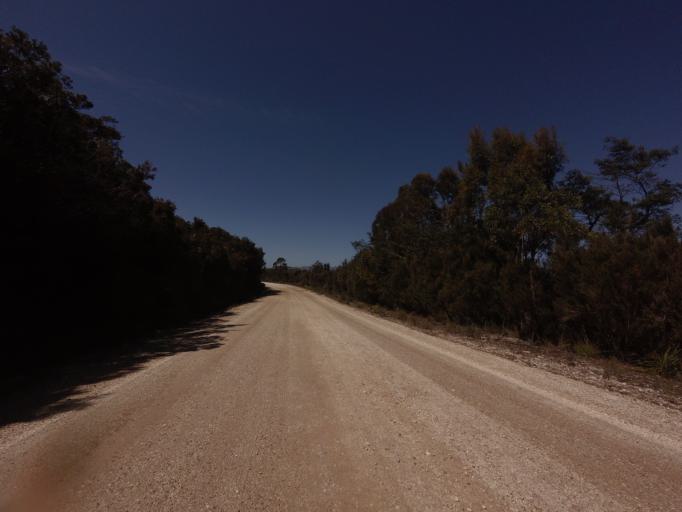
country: AU
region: Tasmania
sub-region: Huon Valley
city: Geeveston
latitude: -43.0341
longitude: 146.3091
